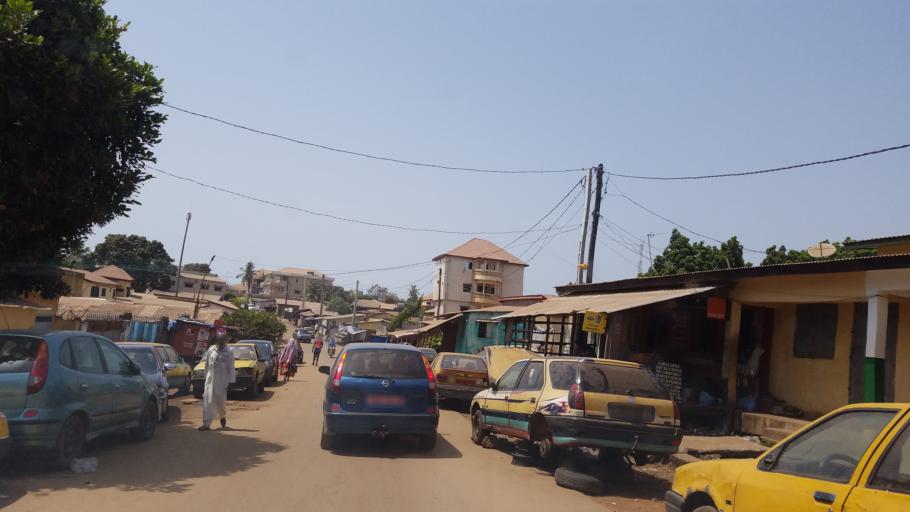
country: GN
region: Conakry
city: Conakry
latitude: 9.5761
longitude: -13.6593
